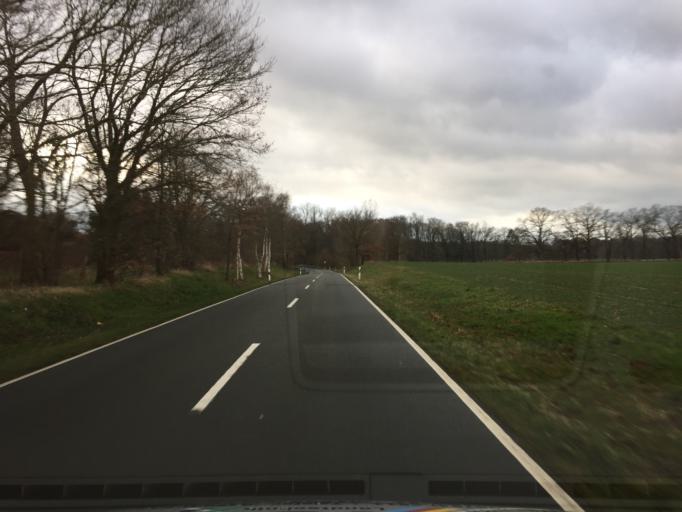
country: DE
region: Lower Saxony
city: Steyerberg
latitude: 52.5357
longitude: 9.0281
